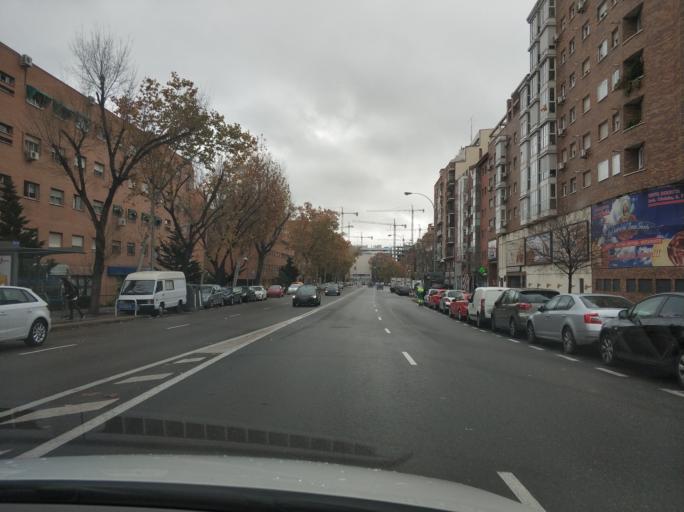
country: ES
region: Madrid
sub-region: Provincia de Madrid
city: Usera
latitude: 40.3875
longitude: -3.6986
